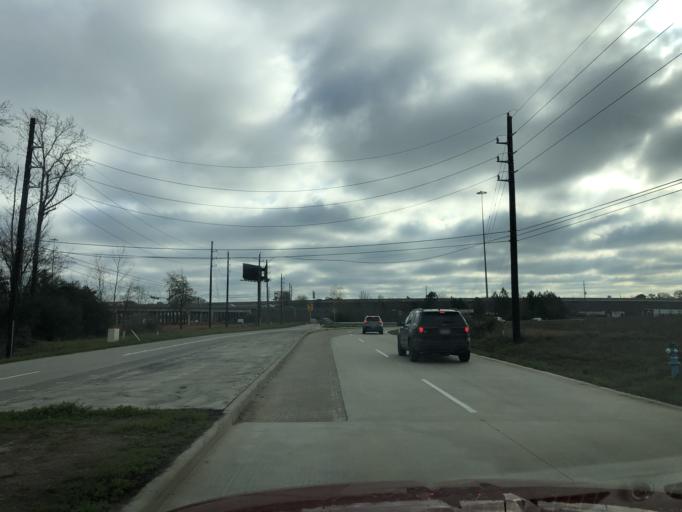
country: US
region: Texas
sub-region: Harris County
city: Spring
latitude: 30.0830
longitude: -95.4398
